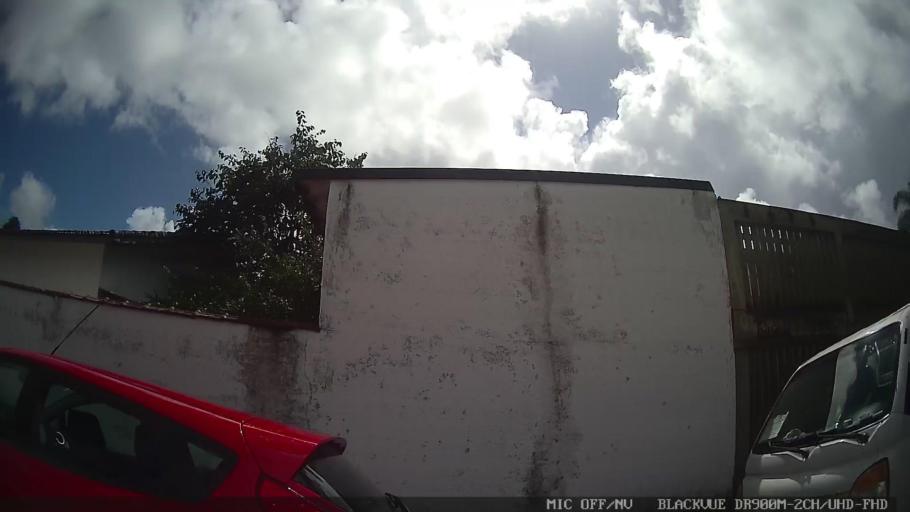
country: BR
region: Sao Paulo
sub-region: Itanhaem
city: Itanhaem
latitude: -24.1926
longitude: -46.8089
